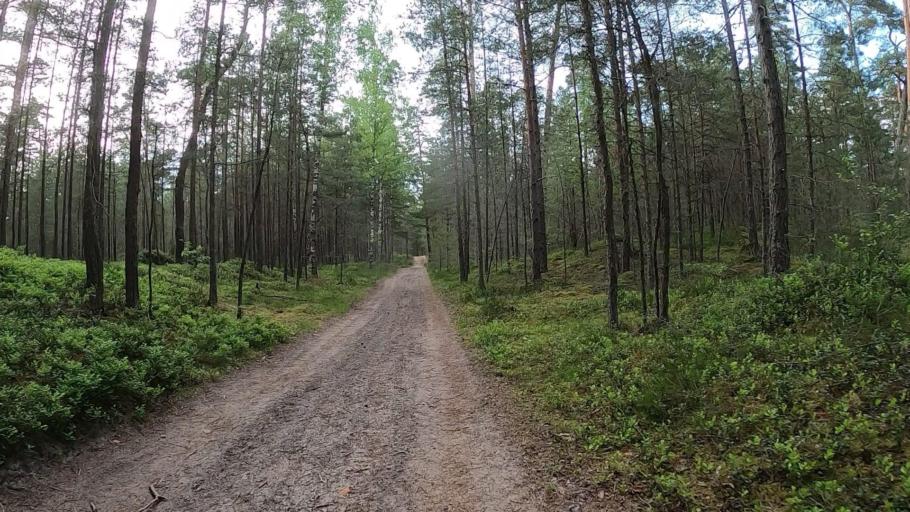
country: LV
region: Riga
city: Jaunciems
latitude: 57.0752
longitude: 24.1311
